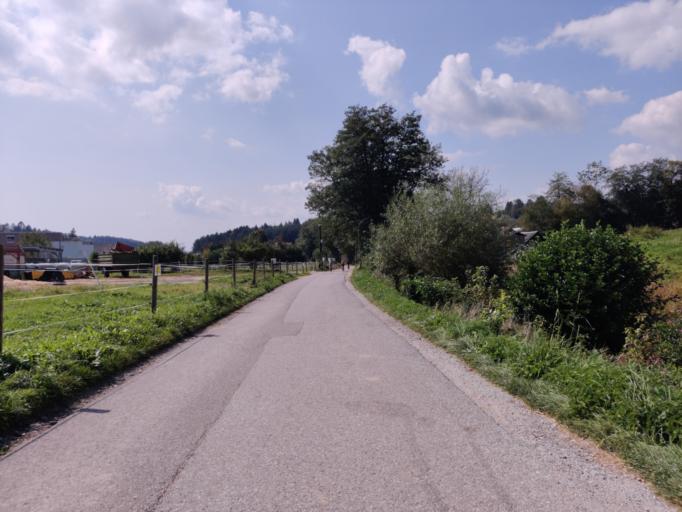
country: AT
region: Styria
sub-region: Politischer Bezirk Graz-Umgebung
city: Kumberg
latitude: 47.1273
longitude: 15.5197
